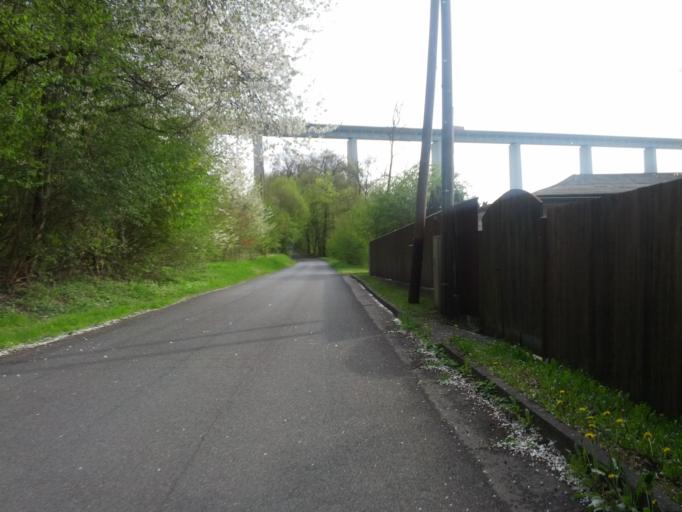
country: DE
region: Thuringia
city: Krauthausen
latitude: 51.0133
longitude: 10.2352
